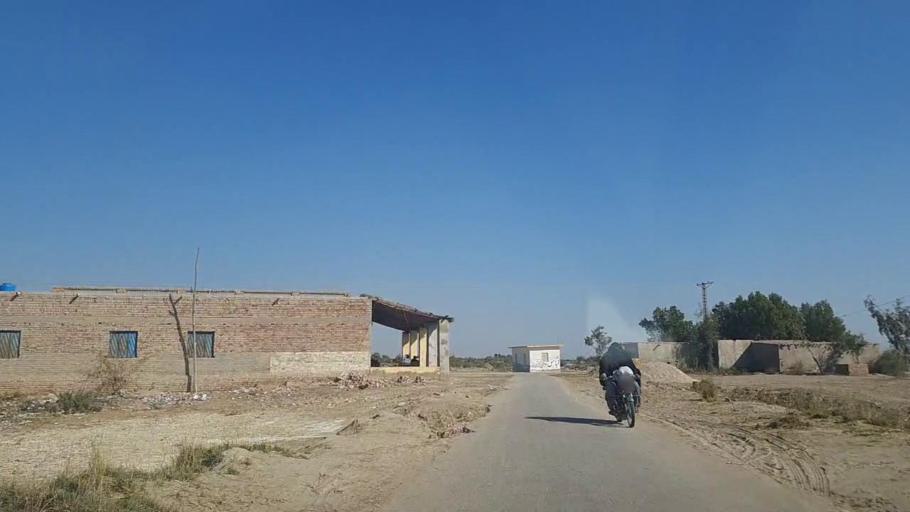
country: PK
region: Sindh
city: Sanghar
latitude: 26.2207
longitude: 68.9521
